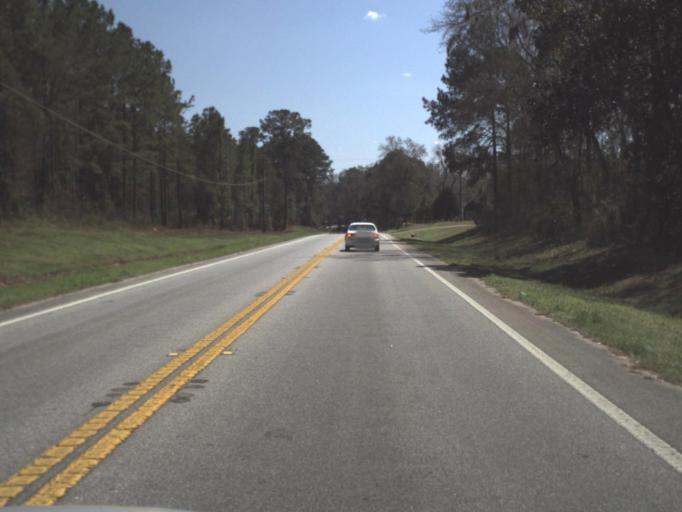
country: US
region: Florida
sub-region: Gadsden County
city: Quincy
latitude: 30.6126
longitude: -84.5903
